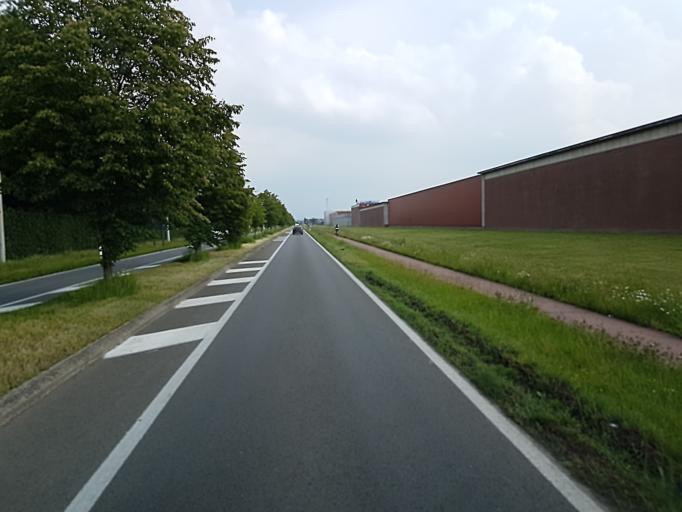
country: BE
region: Flanders
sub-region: Provincie Antwerpen
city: Berlaar
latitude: 51.0984
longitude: 4.6158
